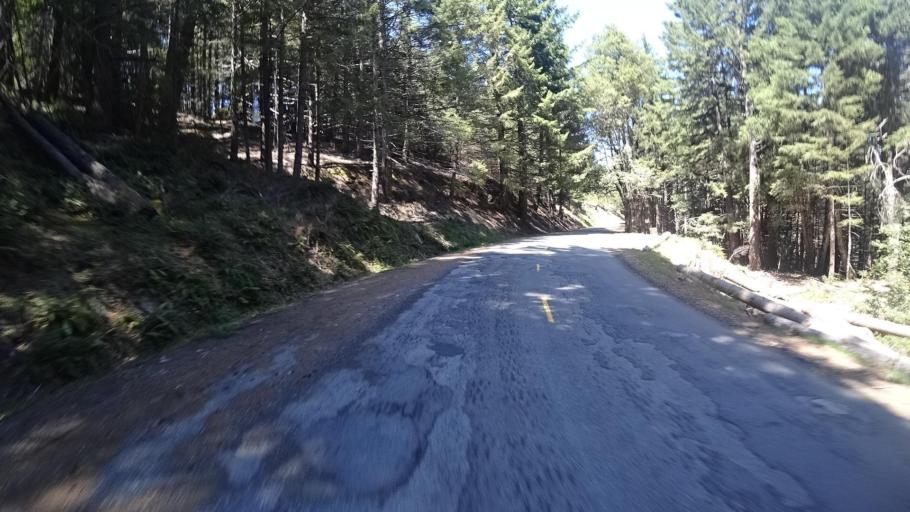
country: US
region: California
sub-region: Humboldt County
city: Rio Dell
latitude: 40.2948
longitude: -124.0575
